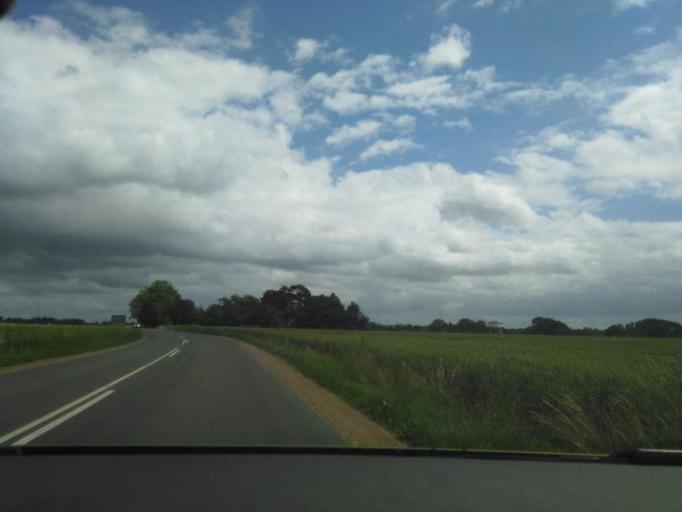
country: DK
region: Zealand
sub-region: Kalundborg Kommune
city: Gorlev
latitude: 55.5465
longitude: 11.2107
